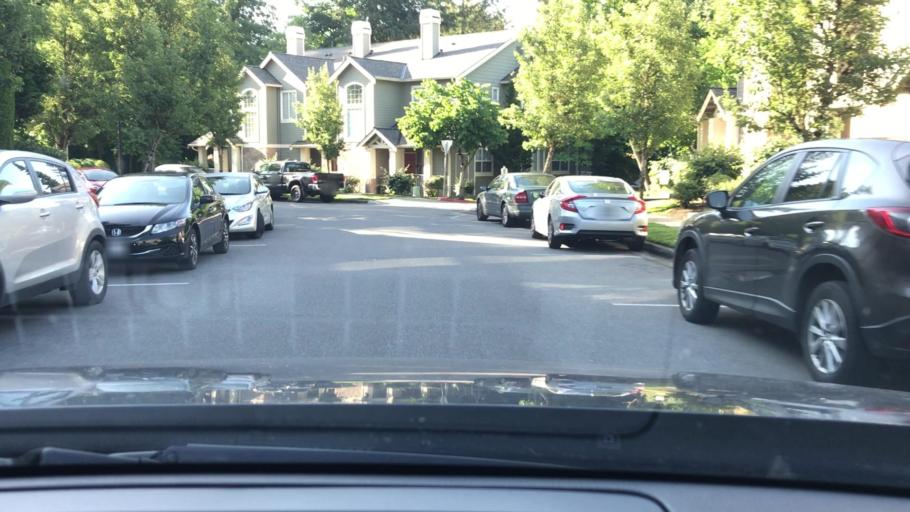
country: US
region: Washington
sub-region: King County
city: Issaquah
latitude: 47.5302
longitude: -122.0710
